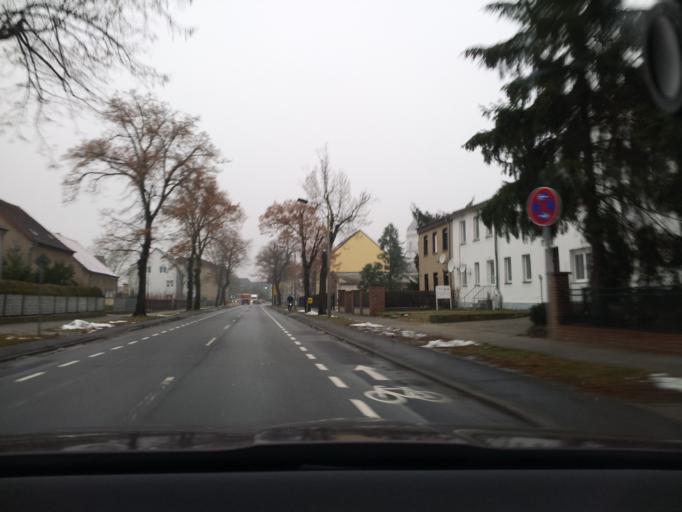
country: DE
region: Brandenburg
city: Furstenwalde
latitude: 52.3565
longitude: 14.0710
